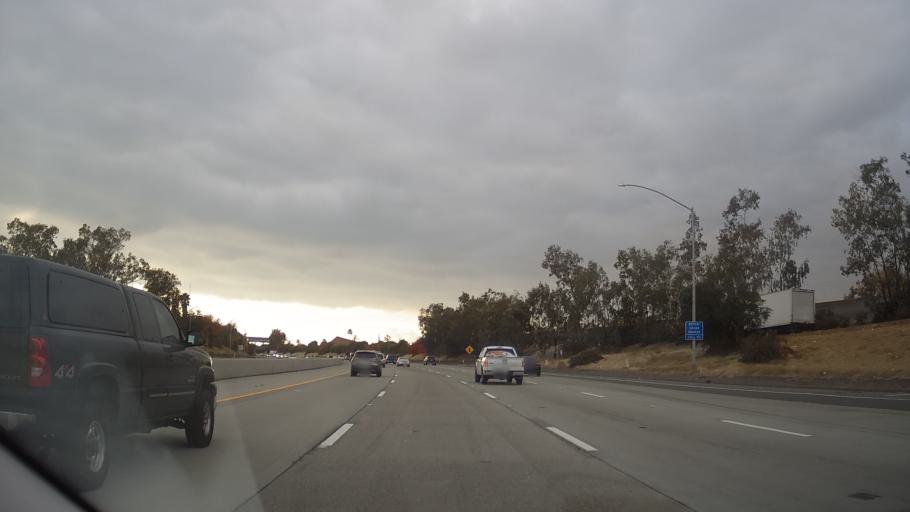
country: US
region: California
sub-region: Sacramento County
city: Rio Linda
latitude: 38.6436
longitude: -121.4302
